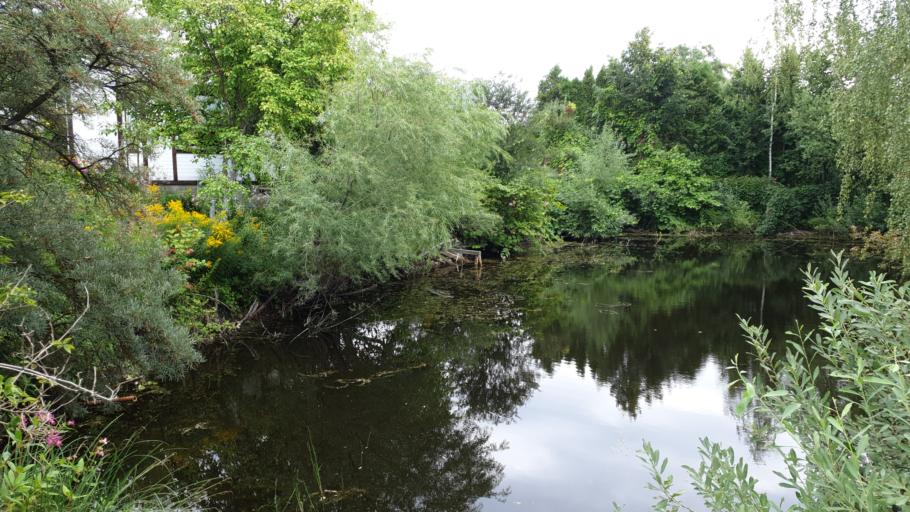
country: LT
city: Grigiskes
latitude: 54.7654
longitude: 25.0256
